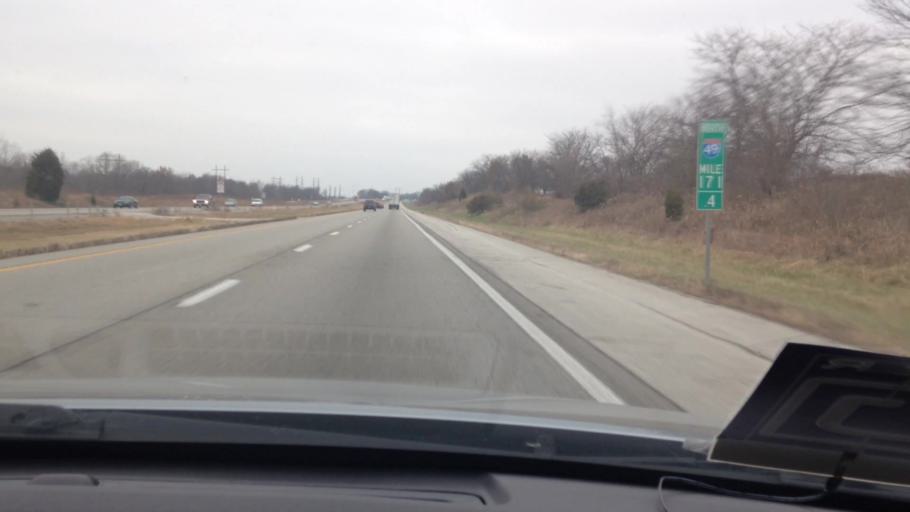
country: US
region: Missouri
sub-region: Cass County
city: Raymore
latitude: 38.7739
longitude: -94.4930
